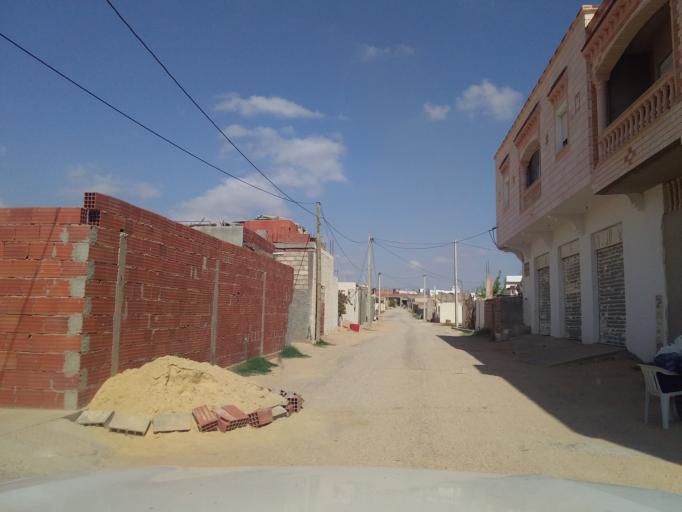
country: TN
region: Madanin
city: Medenine
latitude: 33.5839
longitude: 10.3252
